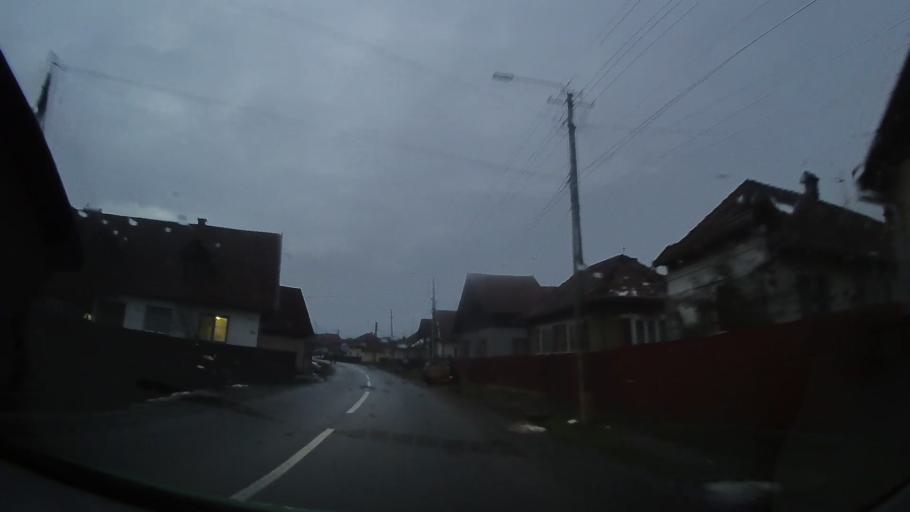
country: RO
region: Harghita
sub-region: Comuna Remetea
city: Remetea
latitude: 46.7927
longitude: 25.4512
